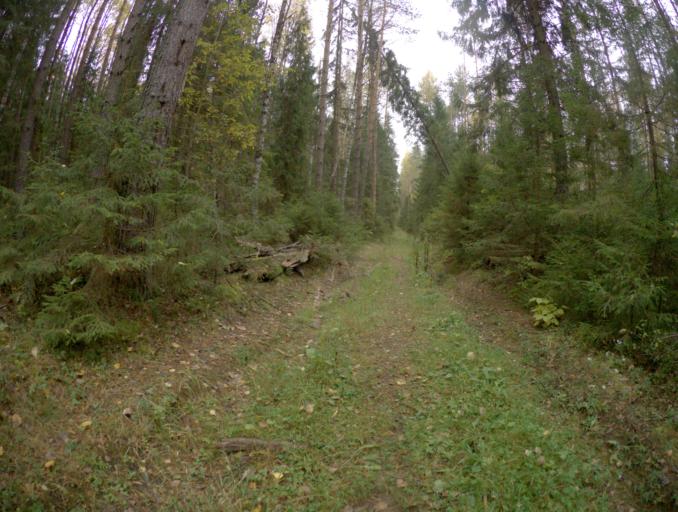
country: RU
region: Vladimir
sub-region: Kovrovskiy Rayon
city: Kovrov
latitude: 56.3361
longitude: 41.4567
